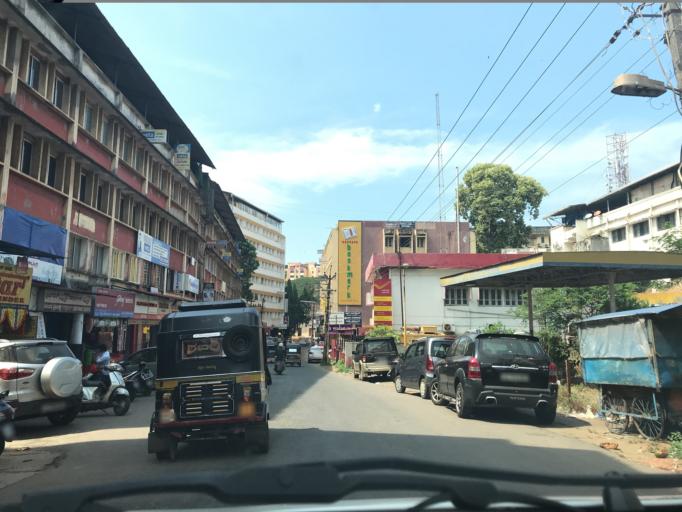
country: IN
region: Karnataka
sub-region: Dakshina Kannada
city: Mangalore
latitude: 12.8694
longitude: 74.8415
